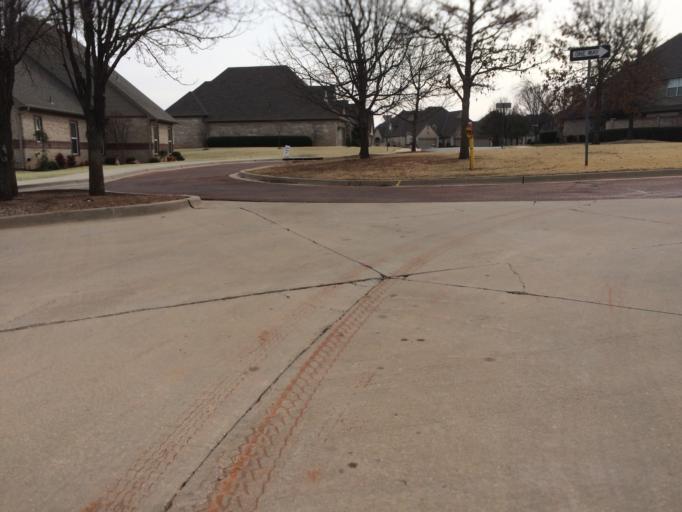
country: US
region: Oklahoma
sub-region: Cleveland County
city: Hall Park
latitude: 35.2168
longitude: -97.4036
